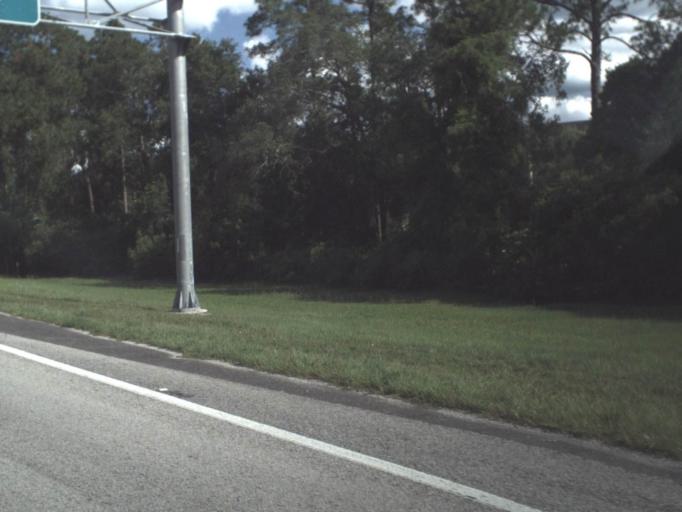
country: US
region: Florida
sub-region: Saint Johns County
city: Ponte Vedra Beach
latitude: 30.2580
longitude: -81.4047
